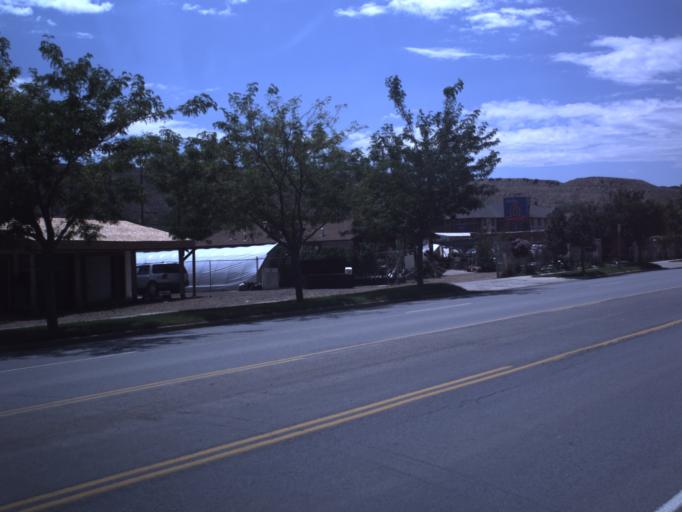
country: US
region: Utah
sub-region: Duchesne County
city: Duchesne
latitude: 40.1635
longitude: -110.4066
